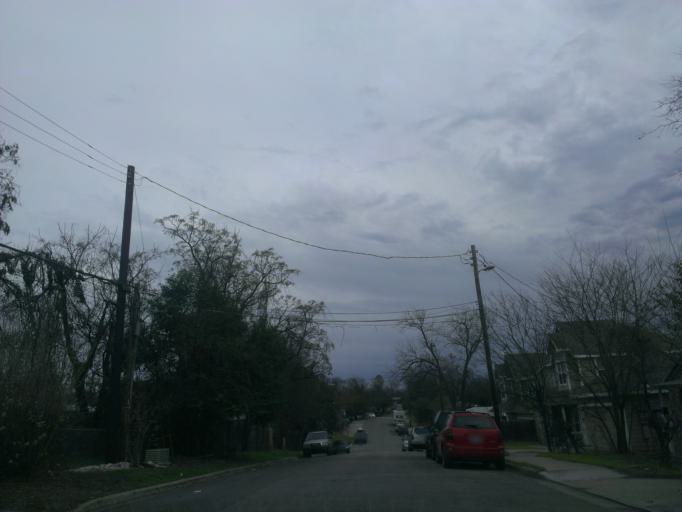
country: US
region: Texas
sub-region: Travis County
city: Austin
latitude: 30.2835
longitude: -97.7178
